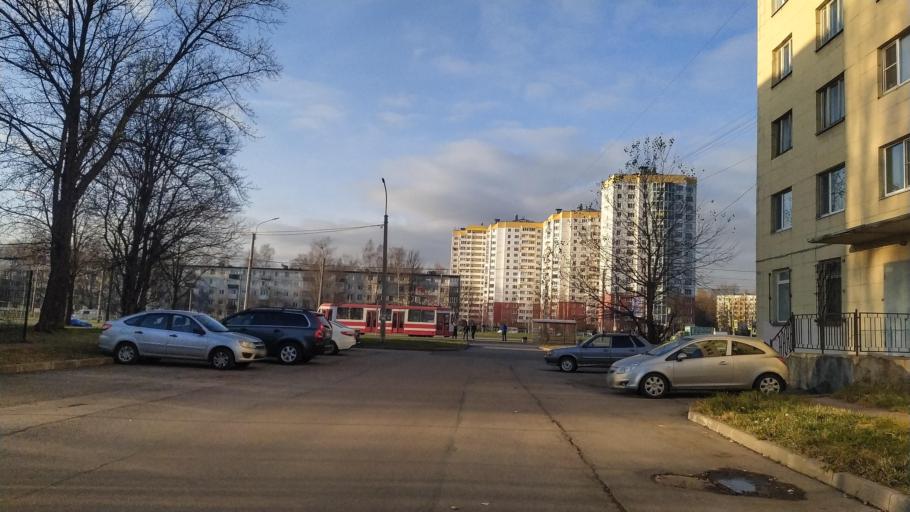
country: RU
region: St.-Petersburg
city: Grazhdanka
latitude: 60.0121
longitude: 30.4357
